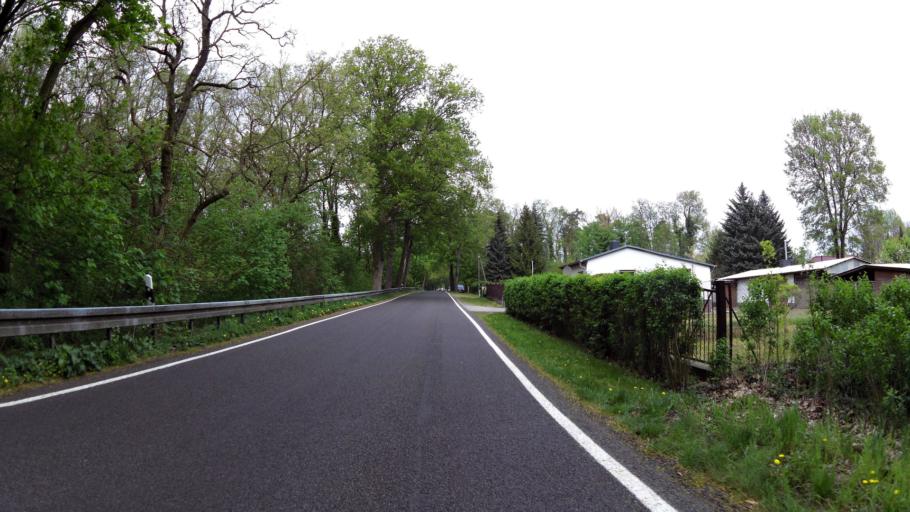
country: DE
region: Brandenburg
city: Mittenwalde
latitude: 52.1988
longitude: 13.5754
